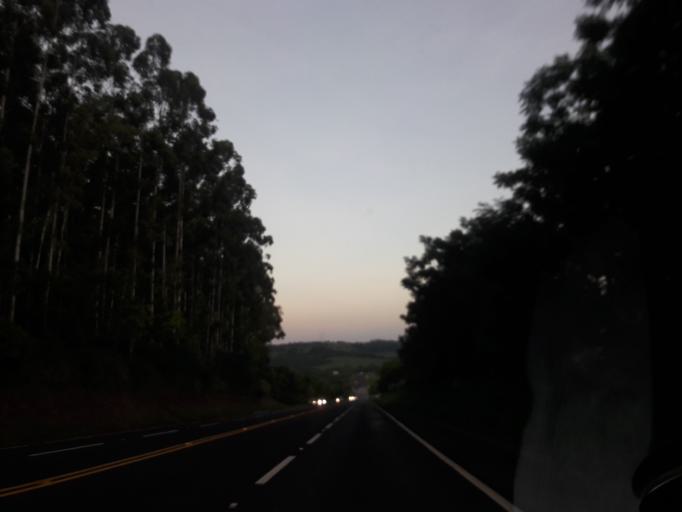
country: BR
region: Parana
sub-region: Mandaguari
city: Mandaguari
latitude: -23.4846
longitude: -51.6214
